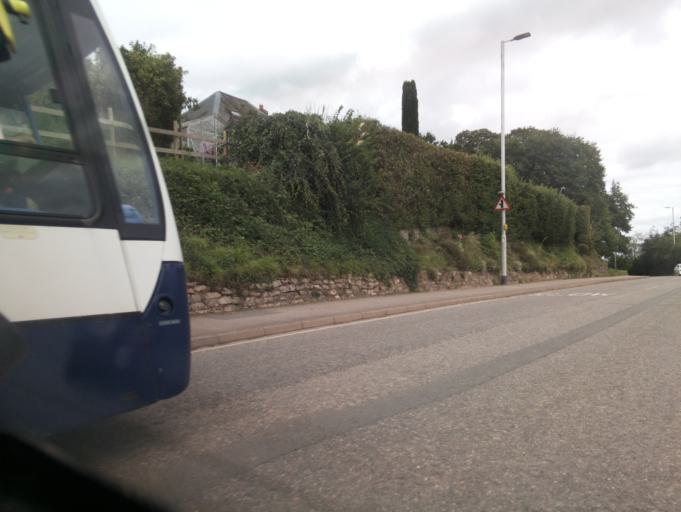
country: GB
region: England
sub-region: Devon
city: Heavitree
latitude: 50.7424
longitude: -3.4669
